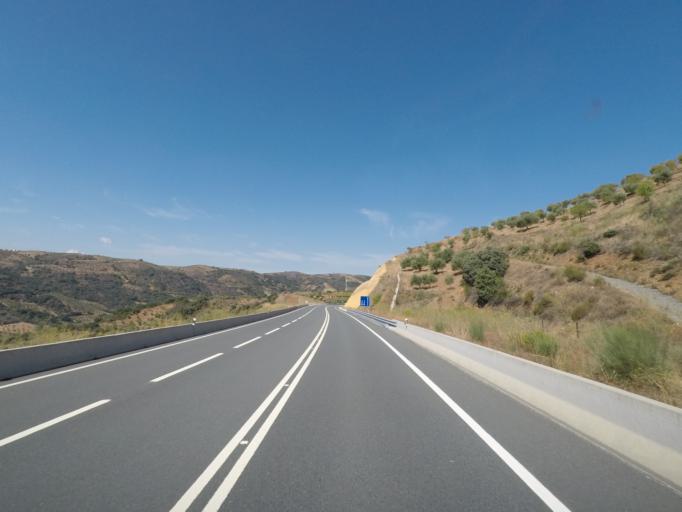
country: PT
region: Braganca
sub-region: Alfandega da Fe
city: Alfandega da Fe
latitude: 41.3038
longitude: -6.9020
